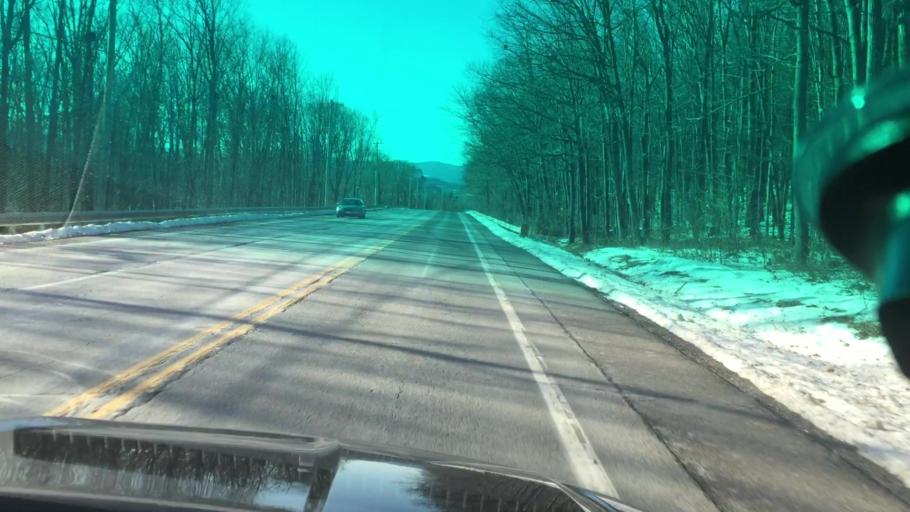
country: US
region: Pennsylvania
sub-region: Luzerne County
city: Oakdale
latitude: 41.0183
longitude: -75.9523
